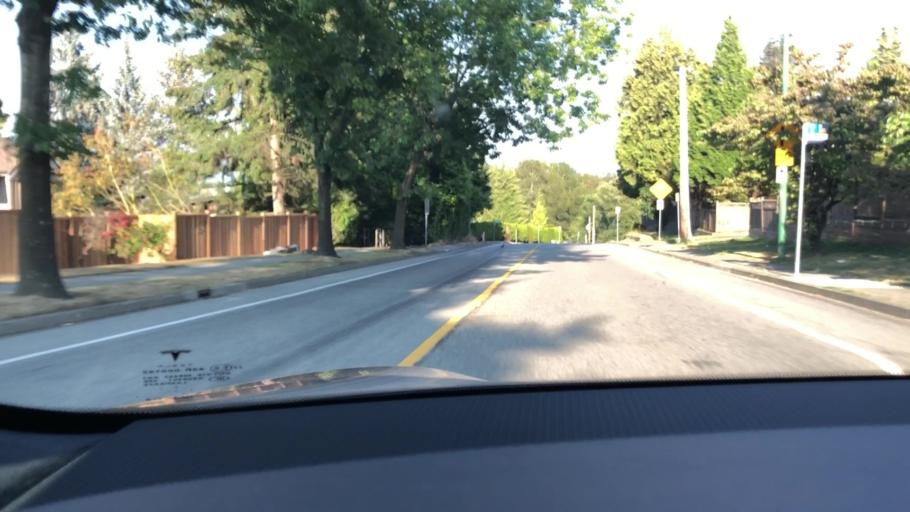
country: CA
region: British Columbia
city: Burnaby
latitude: 49.2296
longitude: -122.9839
